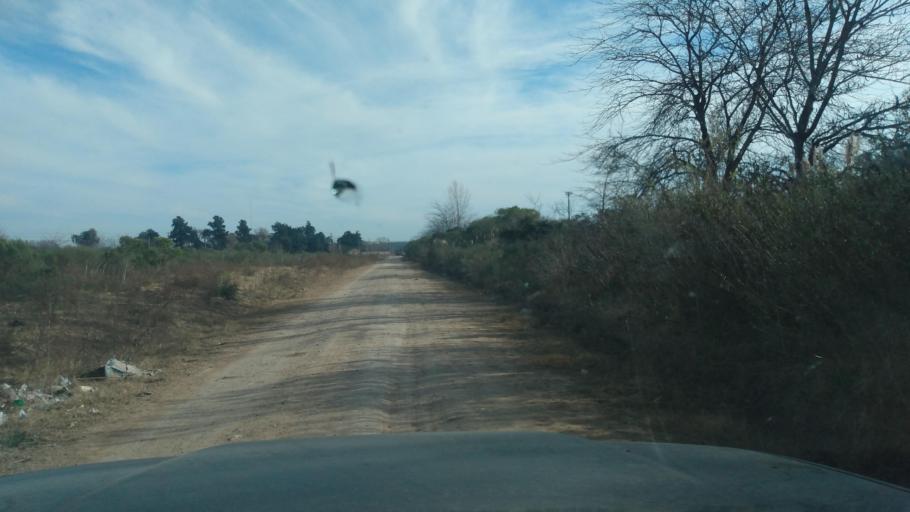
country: AR
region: Buenos Aires
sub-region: Partido de Lujan
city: Lujan
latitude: -34.5355
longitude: -59.1150
